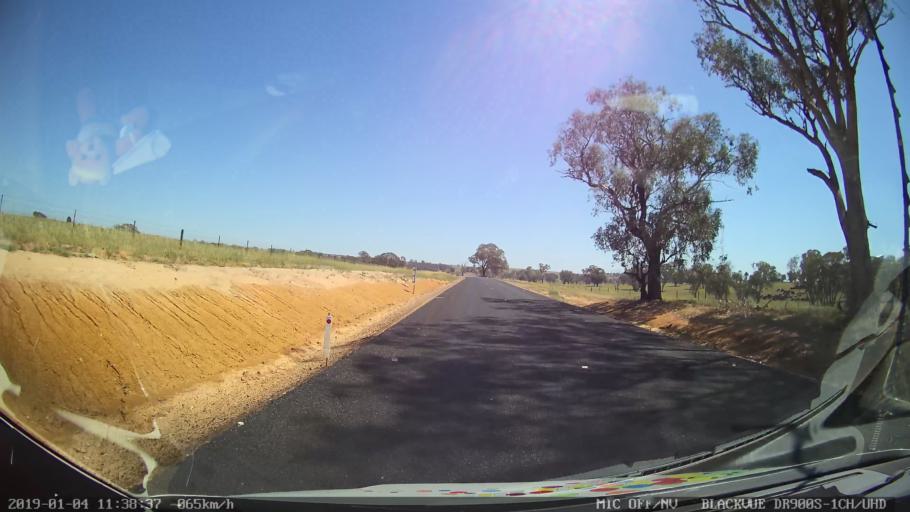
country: AU
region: New South Wales
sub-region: Cabonne
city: Molong
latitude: -33.0212
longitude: 148.8015
